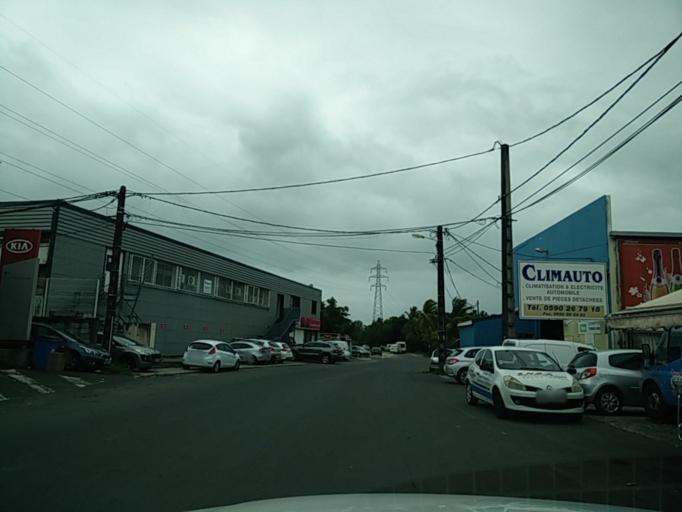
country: GP
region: Guadeloupe
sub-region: Guadeloupe
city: Pointe-a-Pitre
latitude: 16.2531
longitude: -61.5548
